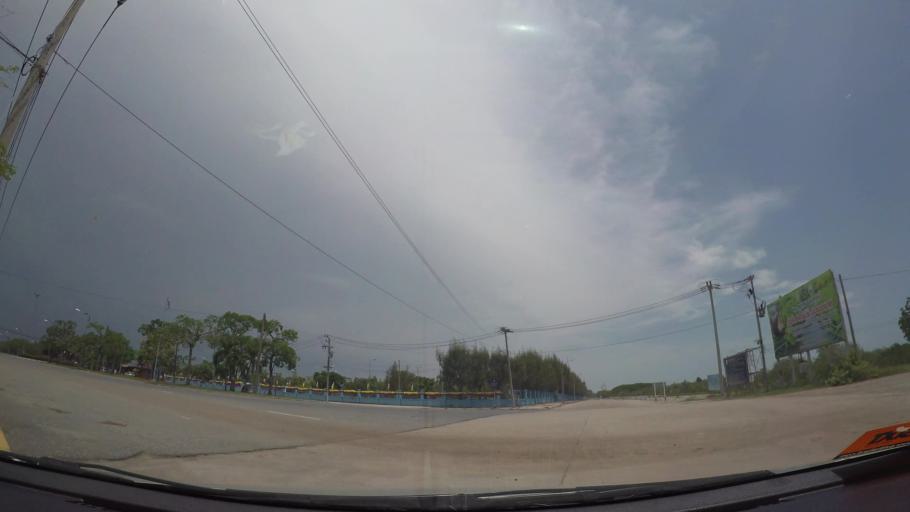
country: TH
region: Chon Buri
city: Chon Buri
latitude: 13.3443
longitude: 100.9499
